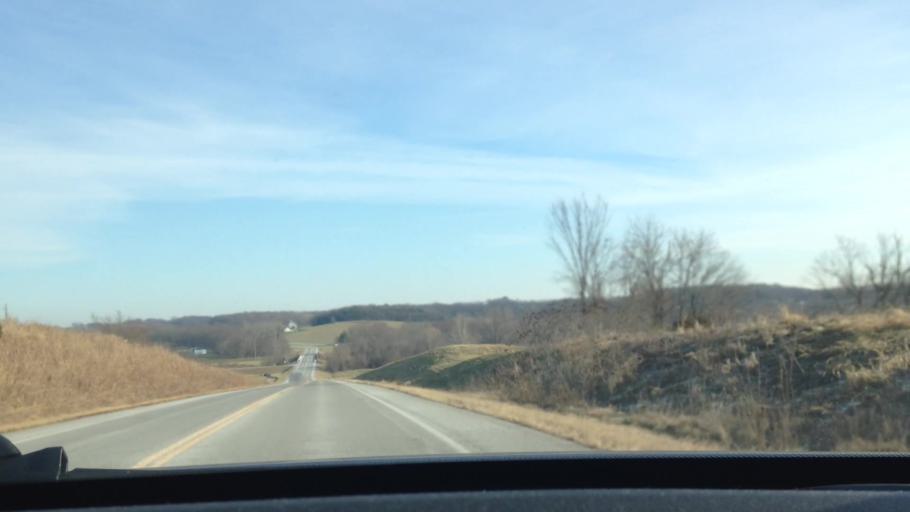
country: US
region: Missouri
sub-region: Platte County
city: Weston
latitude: 39.3914
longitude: -94.8454
